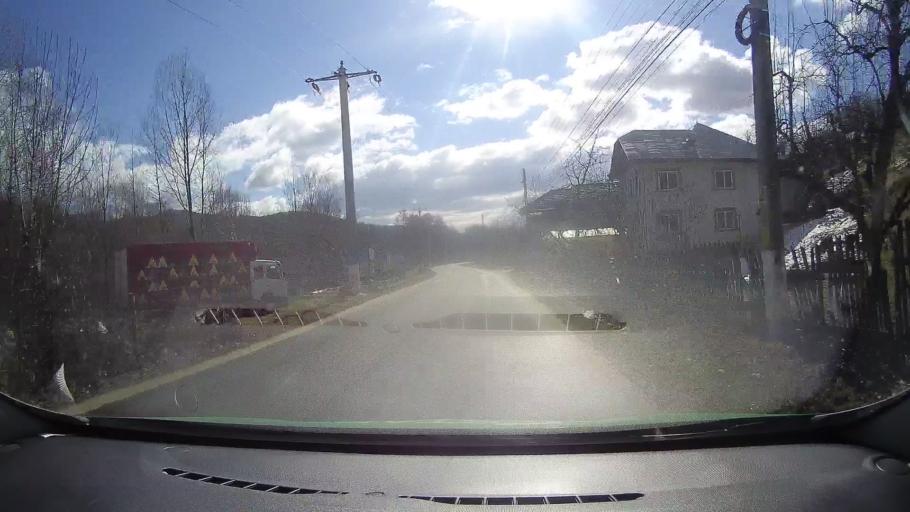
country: RO
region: Dambovita
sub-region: Comuna Runcu
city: Badeni
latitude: 45.1645
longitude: 25.3954
